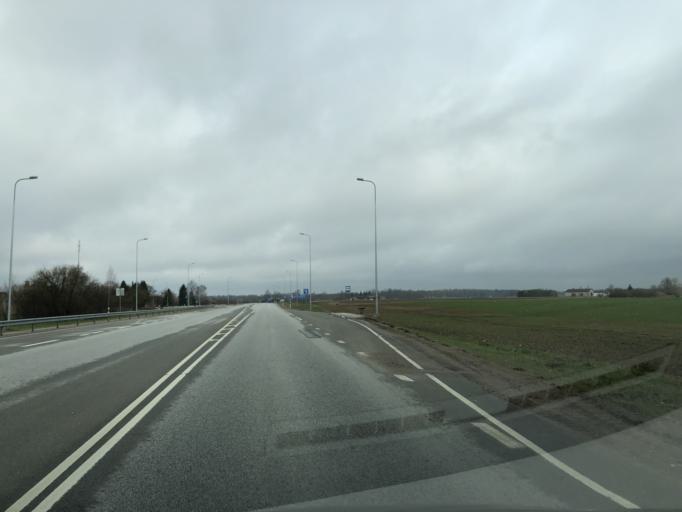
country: EE
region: Jogevamaa
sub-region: Jogeva linn
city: Jogeva
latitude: 58.7493
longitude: 26.3547
